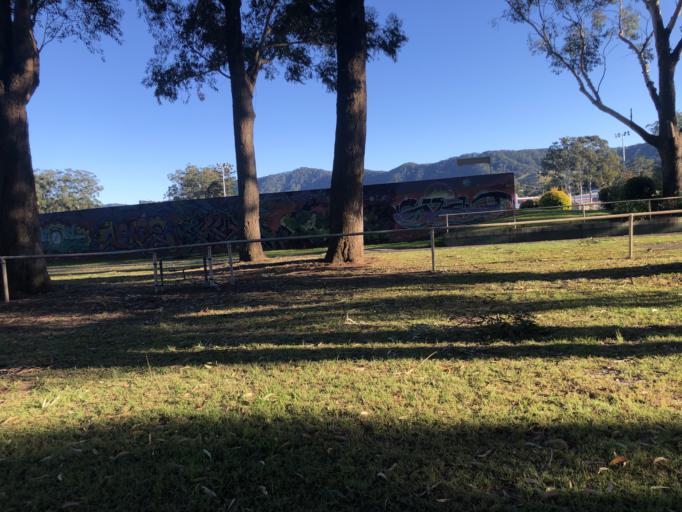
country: AU
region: New South Wales
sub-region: Coffs Harbour
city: Coffs Harbour
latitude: -30.2937
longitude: 153.1204
